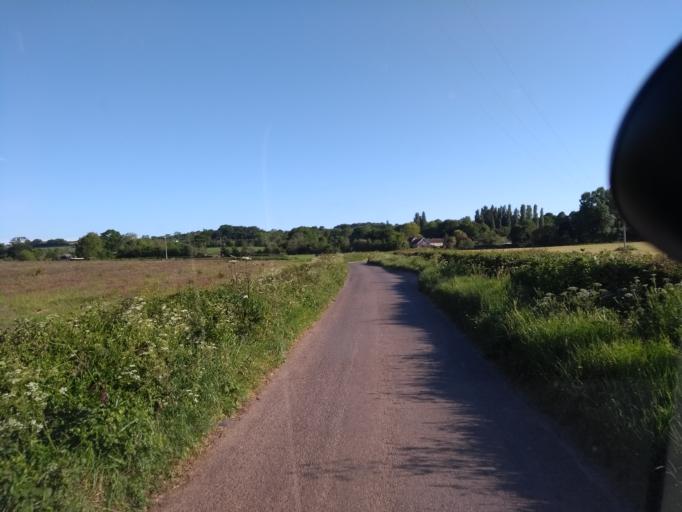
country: GB
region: England
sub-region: Somerset
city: Creech Saint Michael
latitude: 51.0432
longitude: -3.0555
